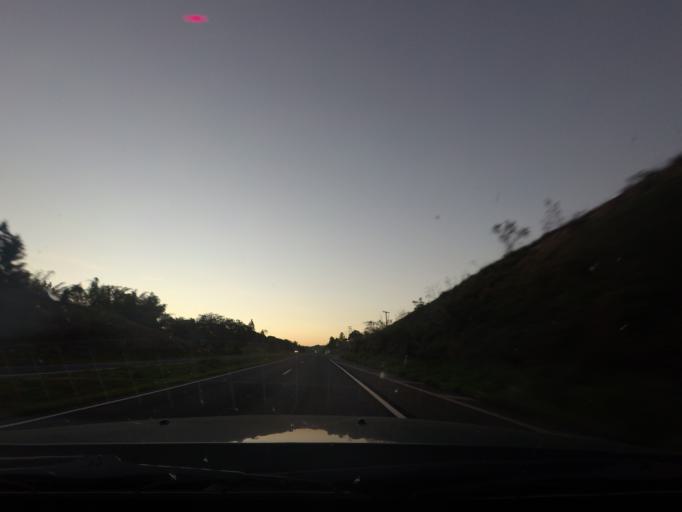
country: BR
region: Sao Paulo
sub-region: Piracicaba
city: Piracicaba
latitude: -22.7358
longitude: -47.5327
